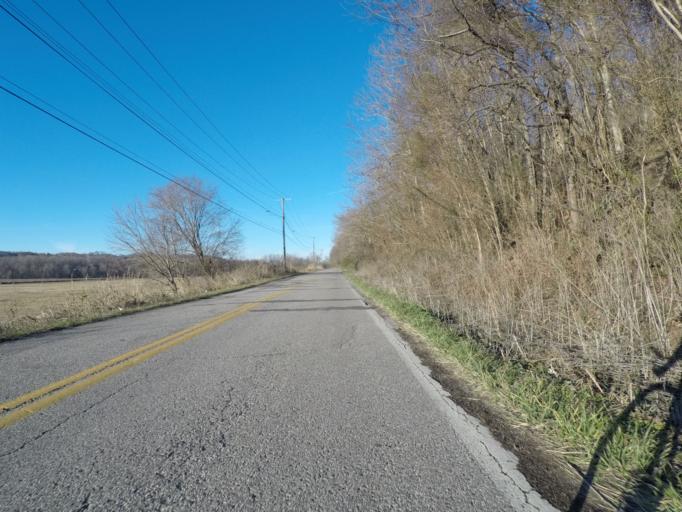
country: US
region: Kentucky
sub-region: Boyd County
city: Catlettsburg
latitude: 38.3906
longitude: -82.5932
